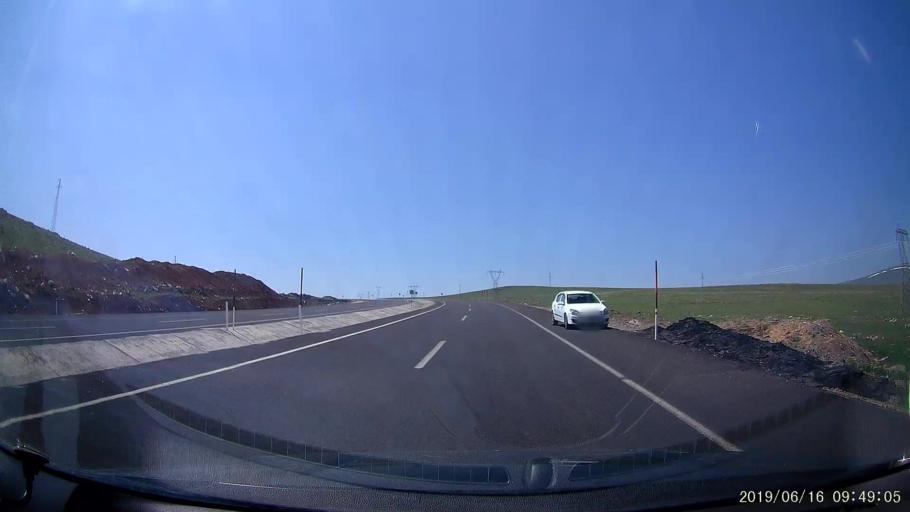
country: TR
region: Kars
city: Digor
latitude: 40.4256
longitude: 43.3563
